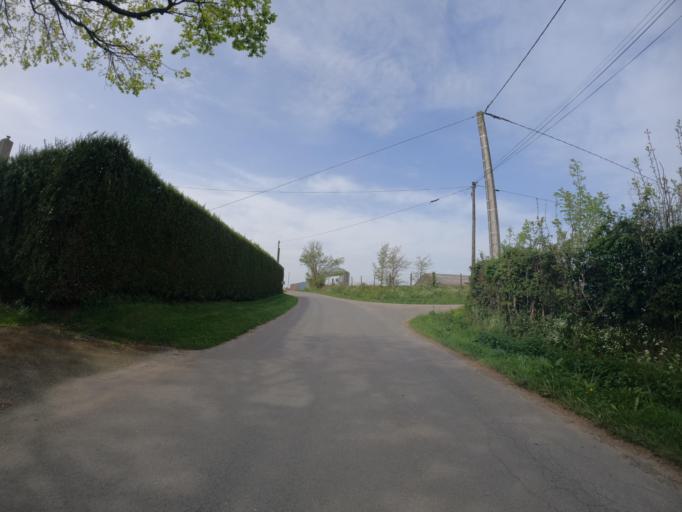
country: FR
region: Poitou-Charentes
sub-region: Departement des Deux-Sevres
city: La Chapelle-Saint-Laurent
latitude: 46.7039
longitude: -0.4970
